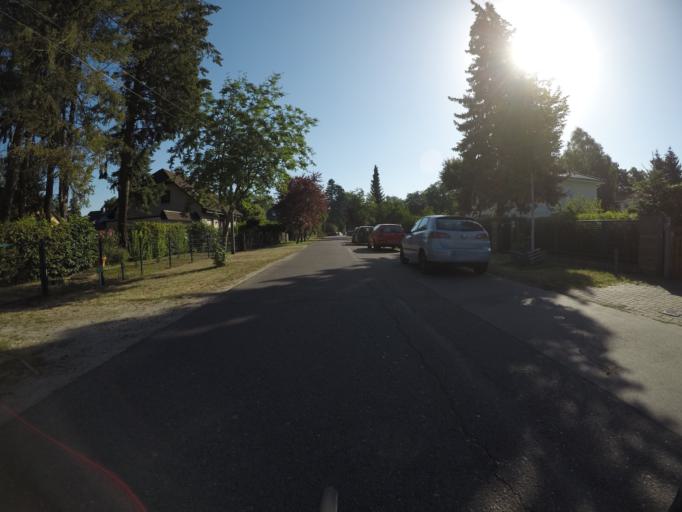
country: DE
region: Berlin
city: Schmockwitz
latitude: 52.3481
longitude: 13.6411
